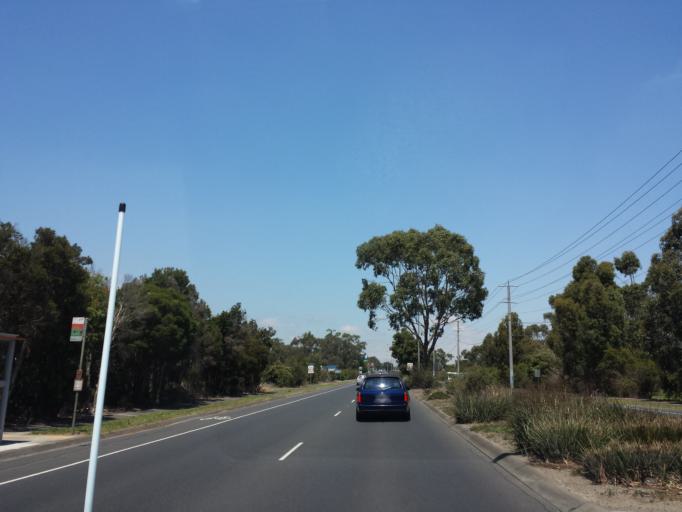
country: AU
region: Victoria
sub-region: Maroondah
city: Bayswater North
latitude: -37.8184
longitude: 145.2879
